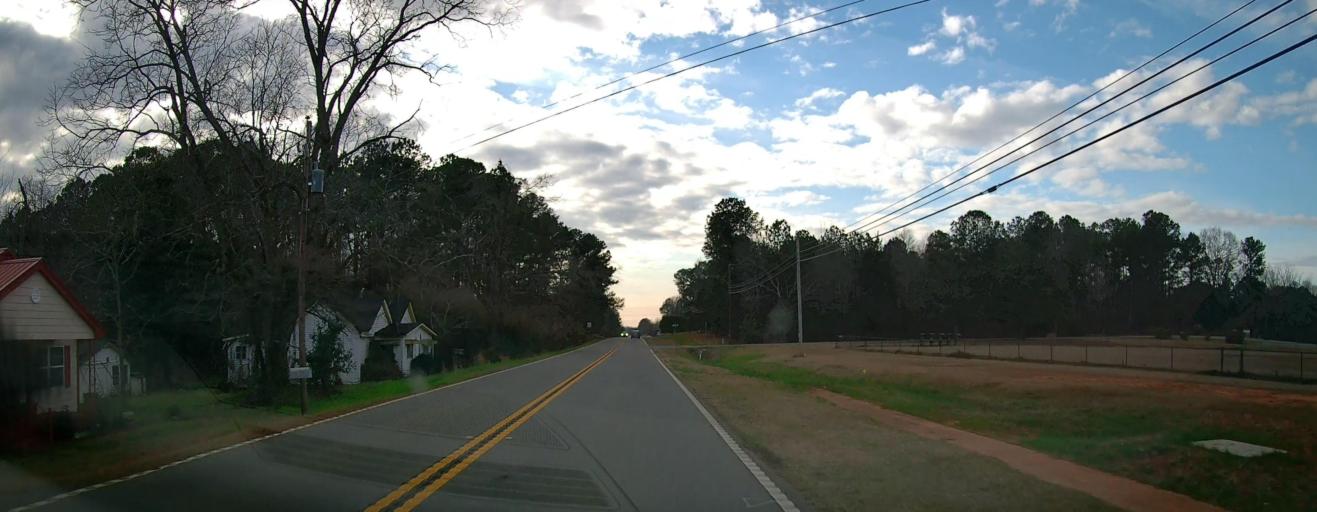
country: US
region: Georgia
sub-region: Harris County
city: Hamilton
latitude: 32.6829
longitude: -84.7492
